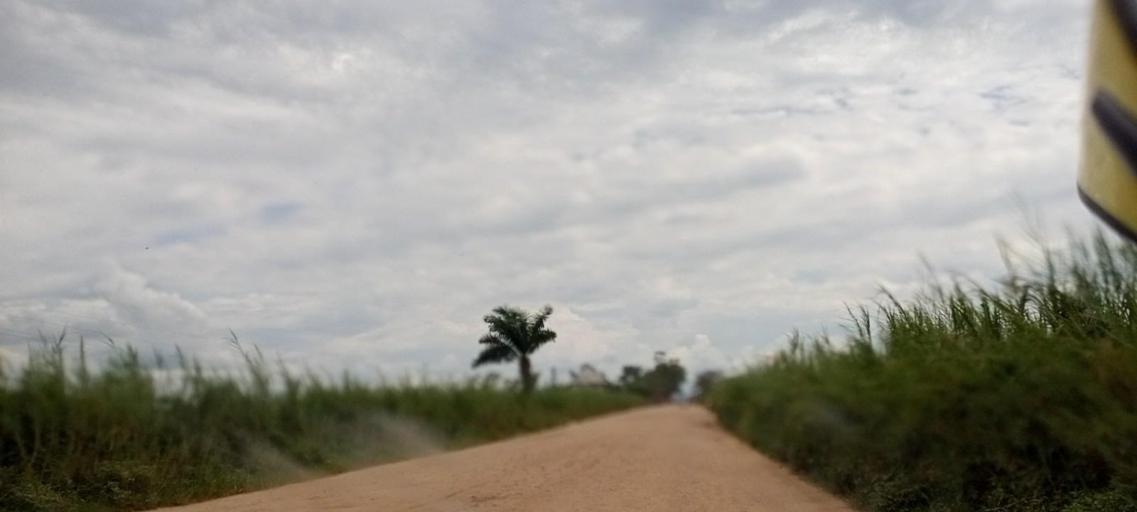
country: CD
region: South Kivu
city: Uvira
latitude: -3.3406
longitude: 29.1995
